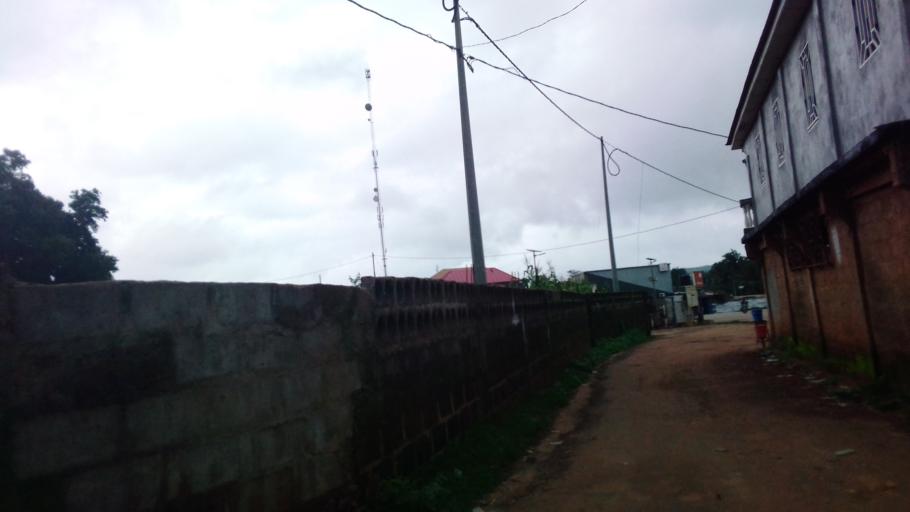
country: SL
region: Northern Province
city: Lunsar
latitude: 8.6880
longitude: -12.5434
